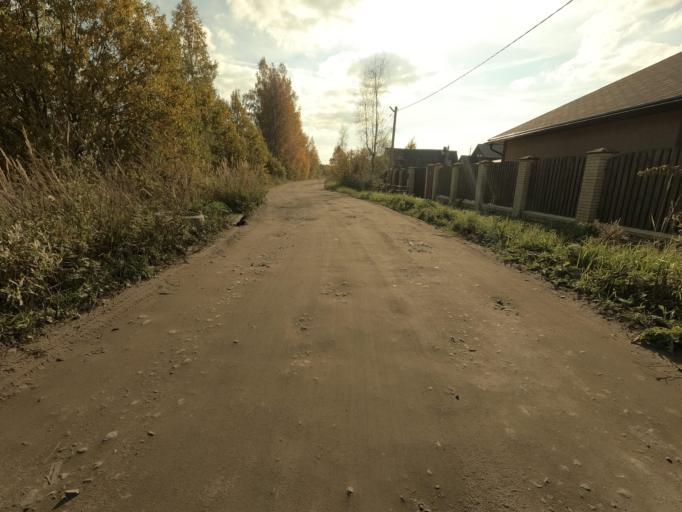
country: RU
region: Leningrad
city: Mga
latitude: 59.7515
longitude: 31.0756
